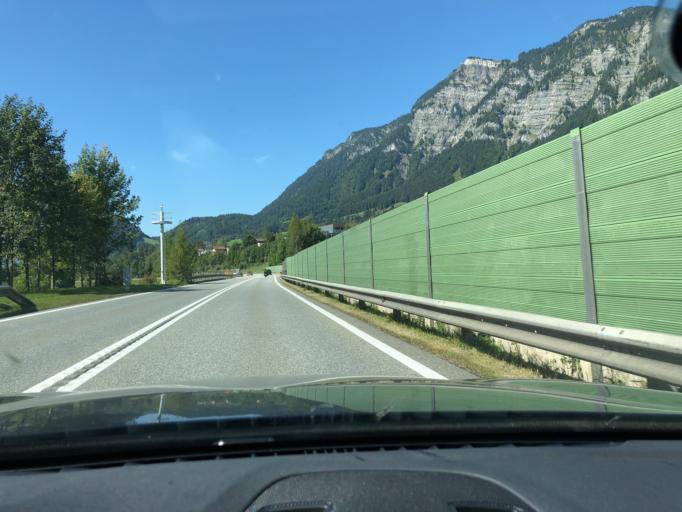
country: AT
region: Vorarlberg
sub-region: Politischer Bezirk Bludenz
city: Innerbraz
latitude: 47.1450
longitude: 9.9018
